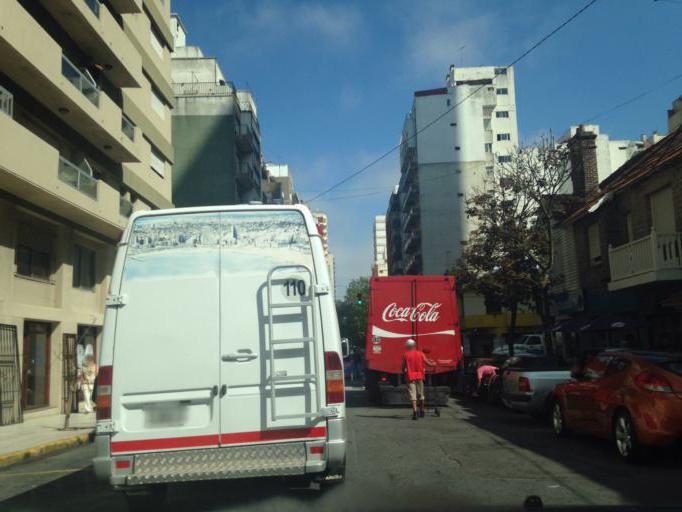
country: AR
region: Buenos Aires
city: Mar del Plata
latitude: -38.0096
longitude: -57.5404
